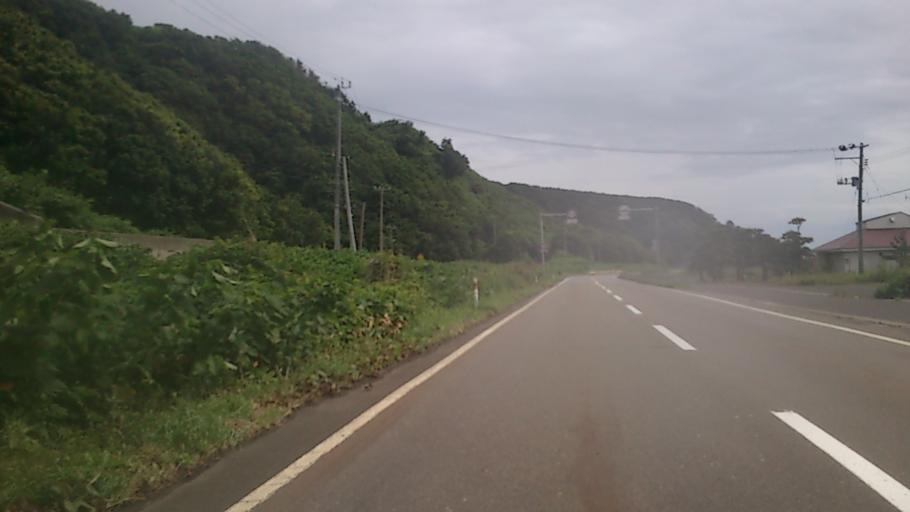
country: JP
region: Akita
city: Noshiromachi
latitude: 40.4552
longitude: 139.9427
